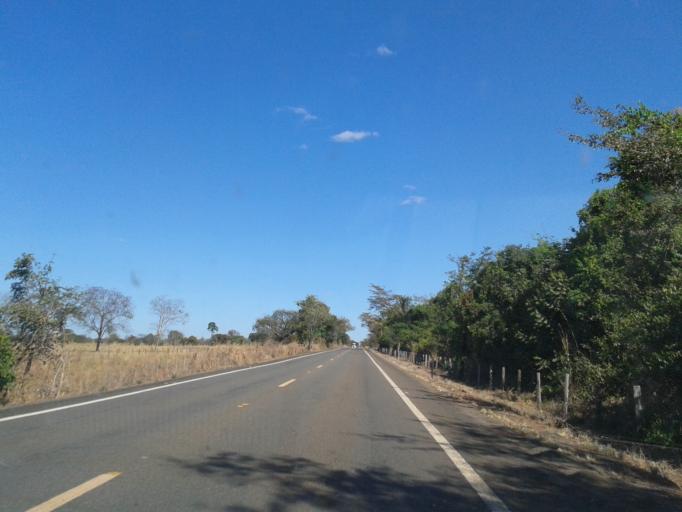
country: BR
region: Goias
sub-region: Sao Miguel Do Araguaia
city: Sao Miguel do Araguaia
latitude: -13.9027
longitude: -50.3262
